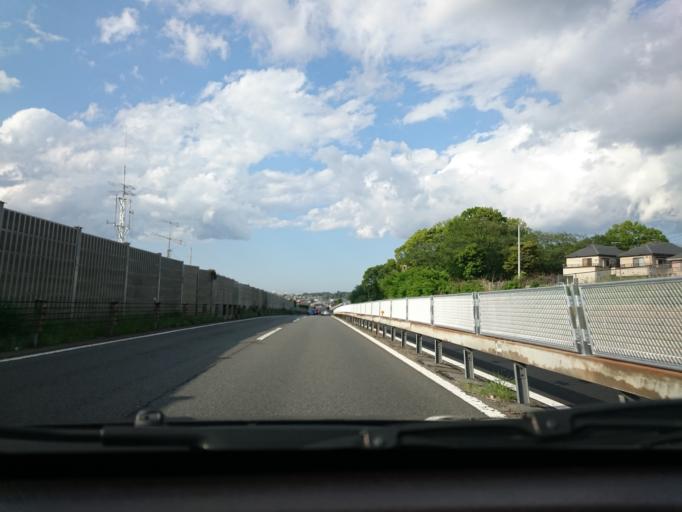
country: JP
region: Kanagawa
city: Isehara
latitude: 35.3534
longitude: 139.2994
